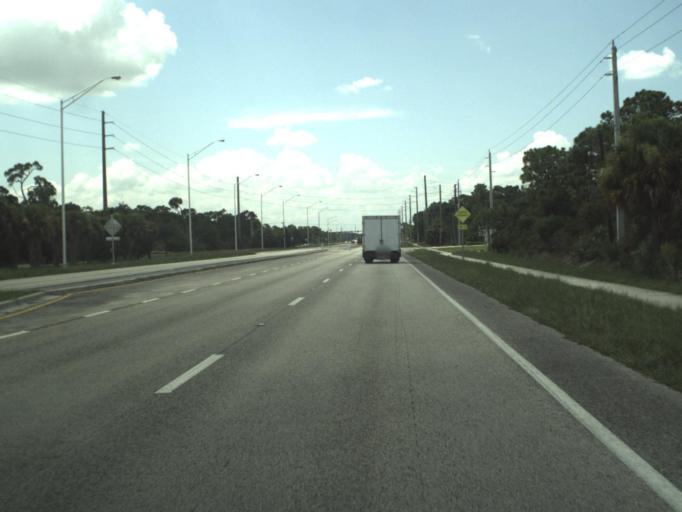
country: US
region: Florida
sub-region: Martin County
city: Port Salerno
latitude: 27.1073
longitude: -80.1677
